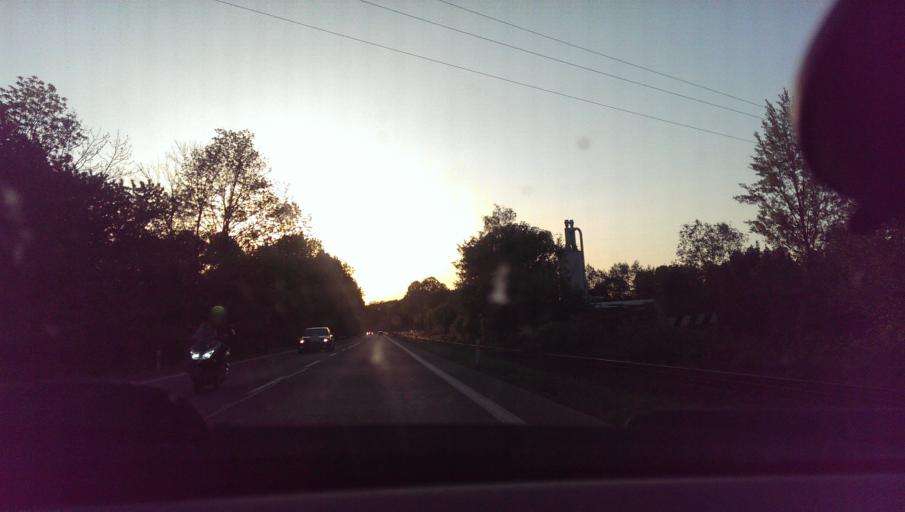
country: CZ
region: Zlin
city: Zubri
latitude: 49.4638
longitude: 18.0687
